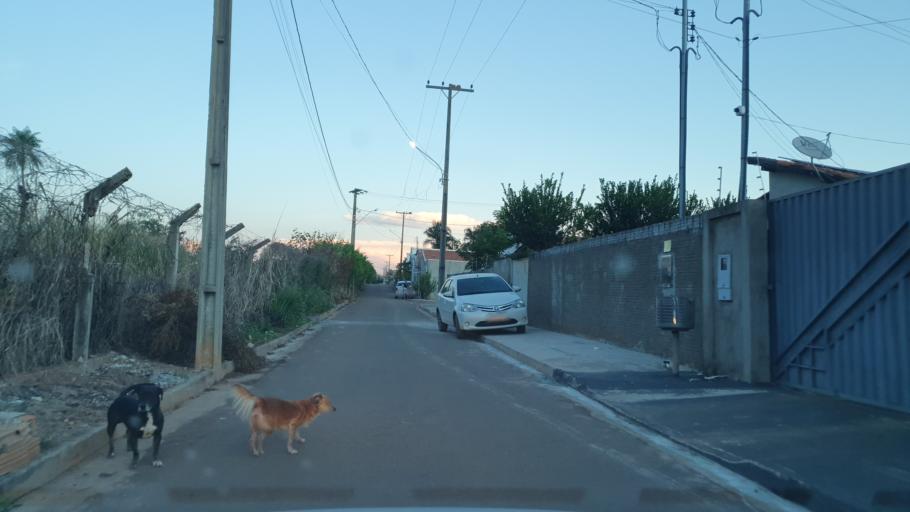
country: BR
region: Mato Grosso
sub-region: Pontes E Lacerda
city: Pontes e Lacerda
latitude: -15.2231
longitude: -59.3280
